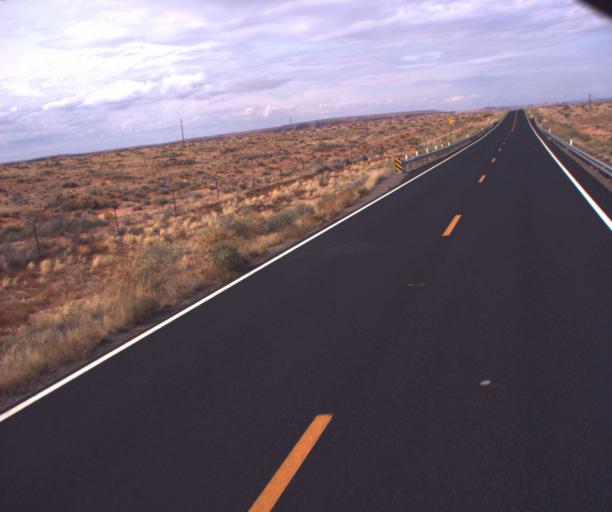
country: US
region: Arizona
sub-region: Apache County
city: Many Farms
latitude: 36.5652
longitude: -109.5435
